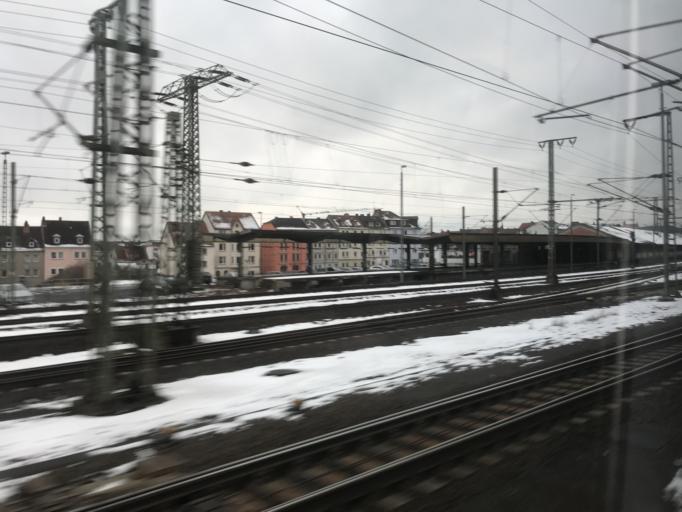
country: DE
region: Hesse
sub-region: Regierungsbezirk Kassel
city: Fulda
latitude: 50.5510
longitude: 9.6904
